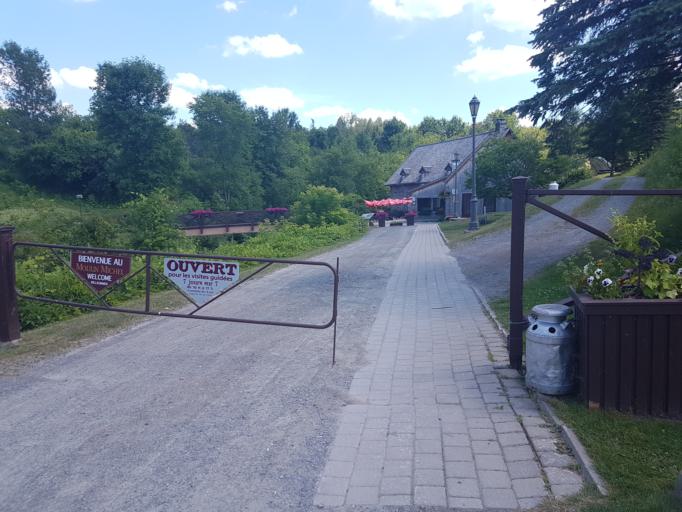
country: CA
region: Quebec
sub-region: Mauricie
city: Becancour
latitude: 46.4133
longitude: -72.2478
